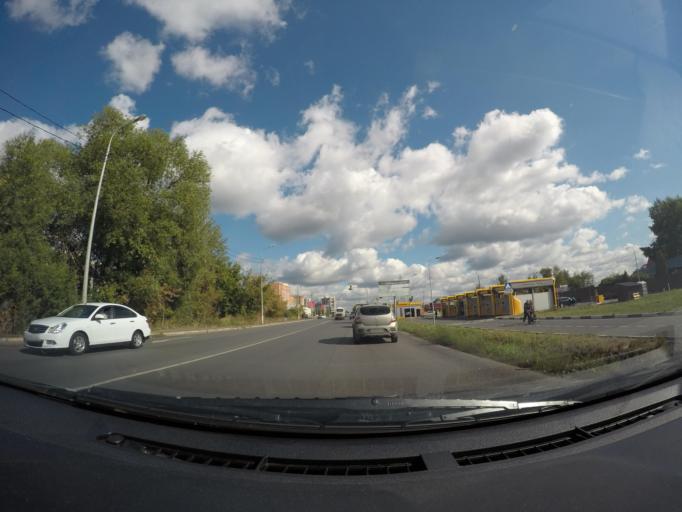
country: RU
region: Moskovskaya
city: Ramenskoye
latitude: 55.5871
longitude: 38.2494
